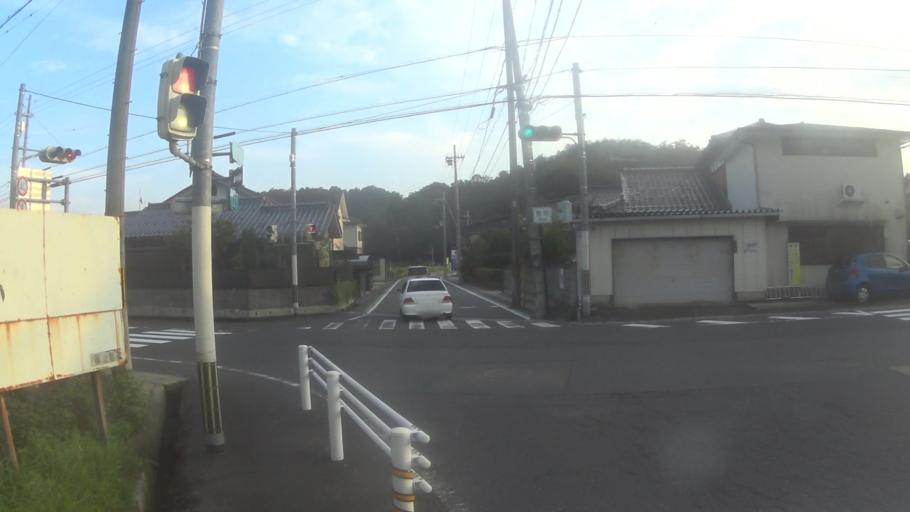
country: JP
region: Kyoto
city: Miyazu
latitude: 35.5307
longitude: 135.0909
